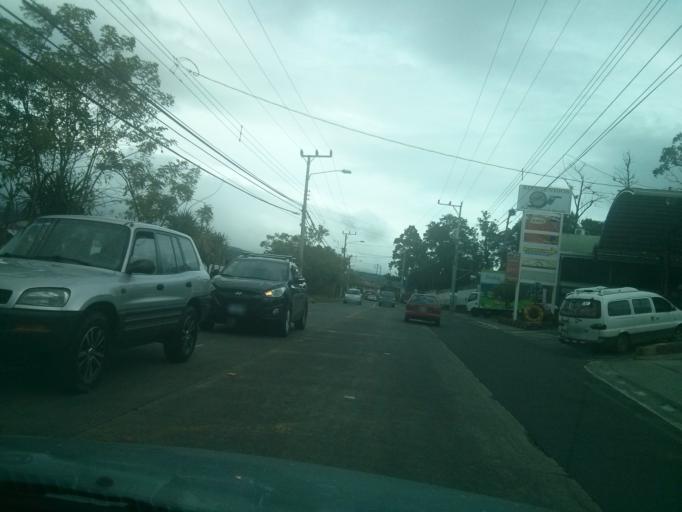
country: CR
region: Heredia
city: San Francisco
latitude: 9.9936
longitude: -84.1303
